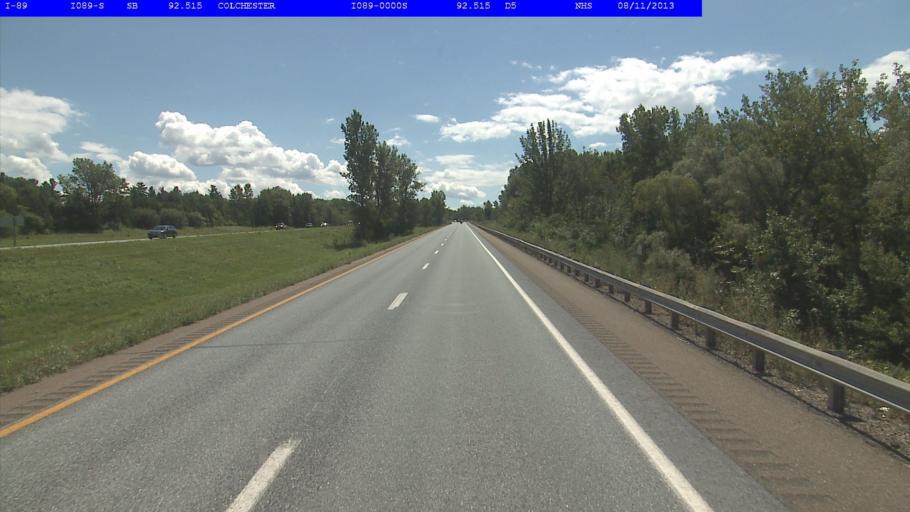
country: US
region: Vermont
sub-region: Chittenden County
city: Winooski
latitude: 44.5173
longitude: -73.1924
